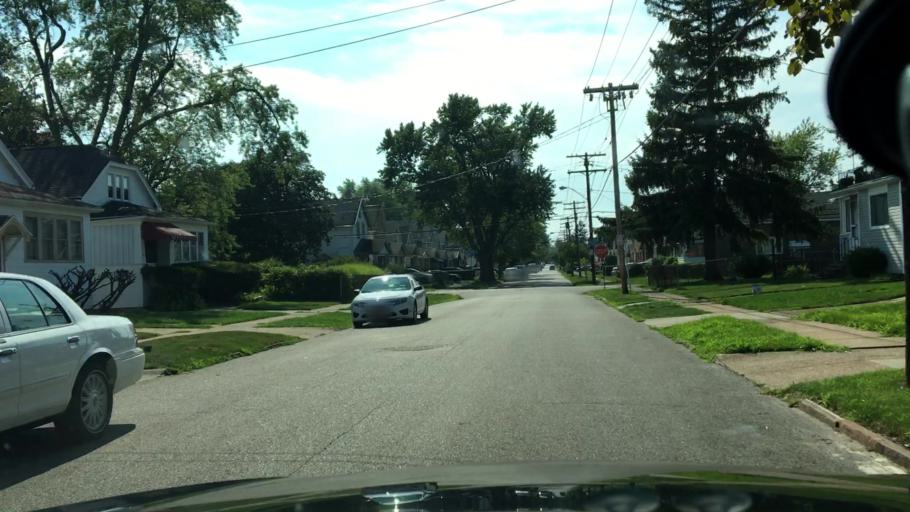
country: US
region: New York
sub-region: Erie County
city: Eggertsville
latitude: 42.9366
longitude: -78.8060
